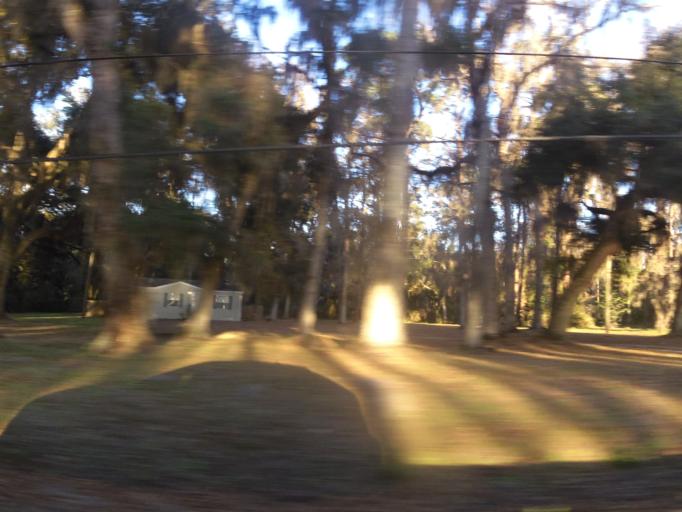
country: US
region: Florida
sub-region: Putnam County
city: East Palatka
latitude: 29.8231
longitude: -81.5525
